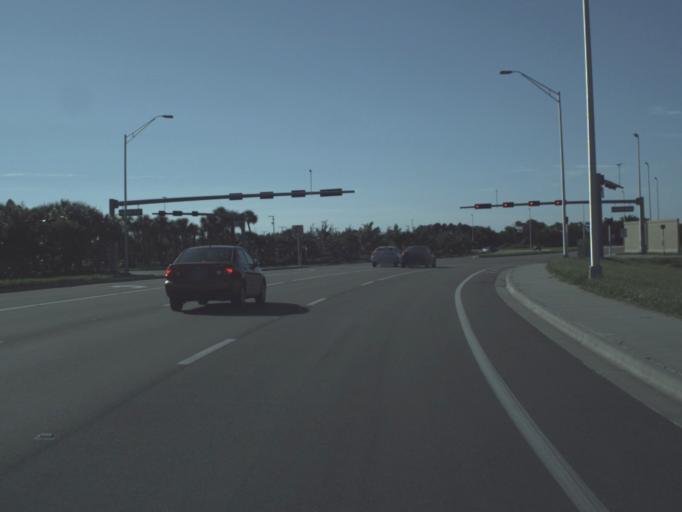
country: US
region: Florida
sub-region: Lee County
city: Fort Myers
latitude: 26.6185
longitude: -81.8601
